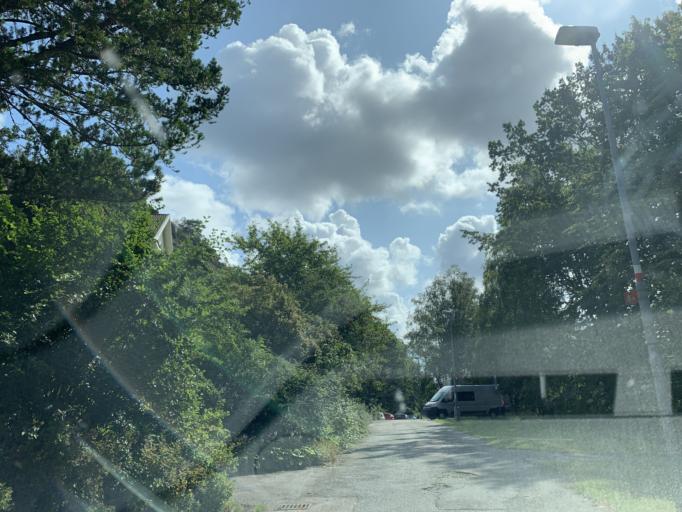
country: SE
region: Vaestra Goetaland
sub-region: Goteborg
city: Eriksbo
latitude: 57.7429
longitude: 12.0606
